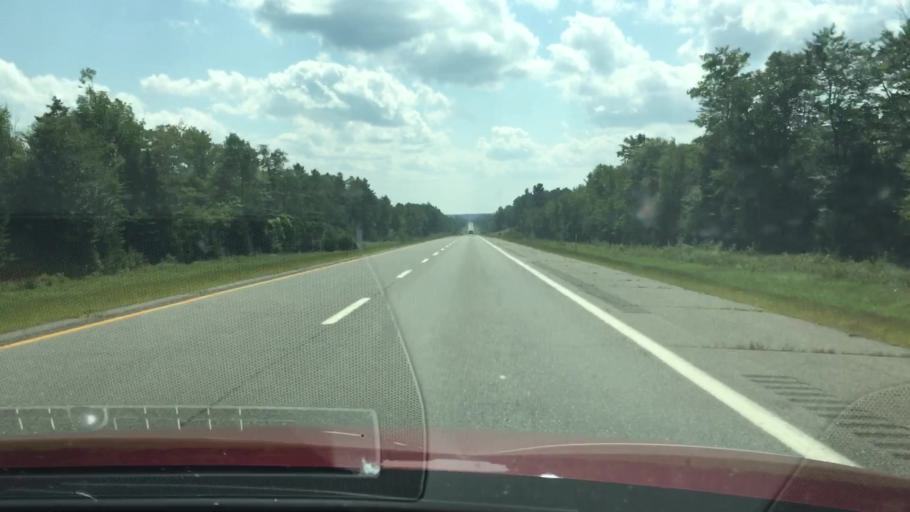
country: US
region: Maine
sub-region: Penobscot County
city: Lincoln
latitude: 45.4164
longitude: -68.5931
